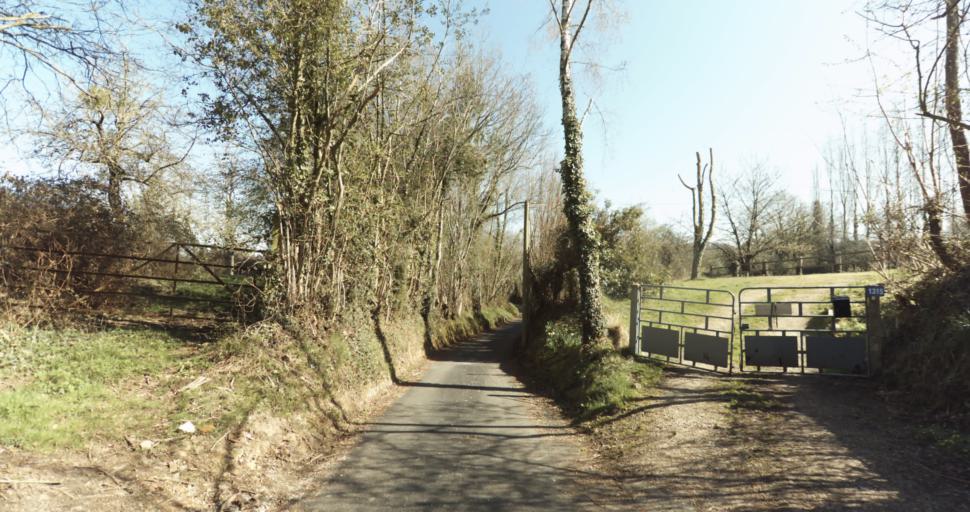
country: FR
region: Lower Normandy
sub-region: Departement du Calvados
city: Livarot
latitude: 48.9843
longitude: 0.0700
